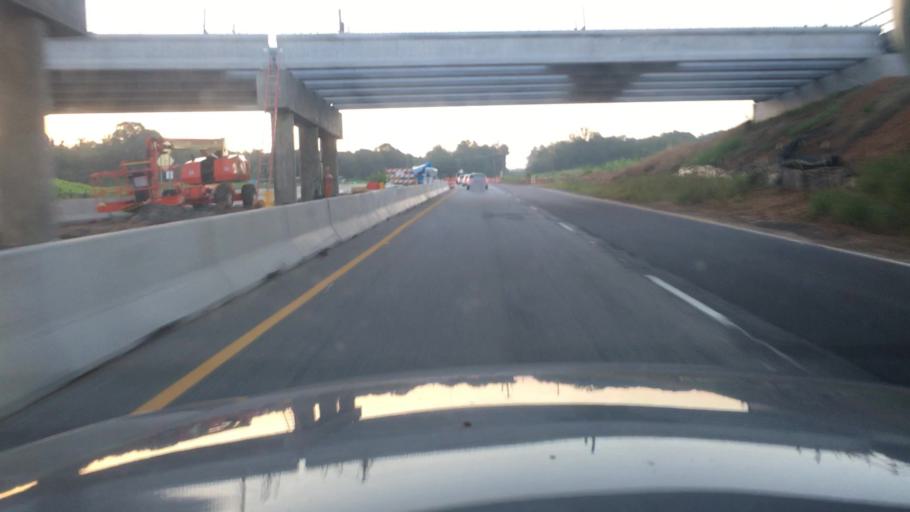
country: US
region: North Carolina
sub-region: Cumberland County
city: Fort Bragg
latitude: 35.0640
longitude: -79.0240
